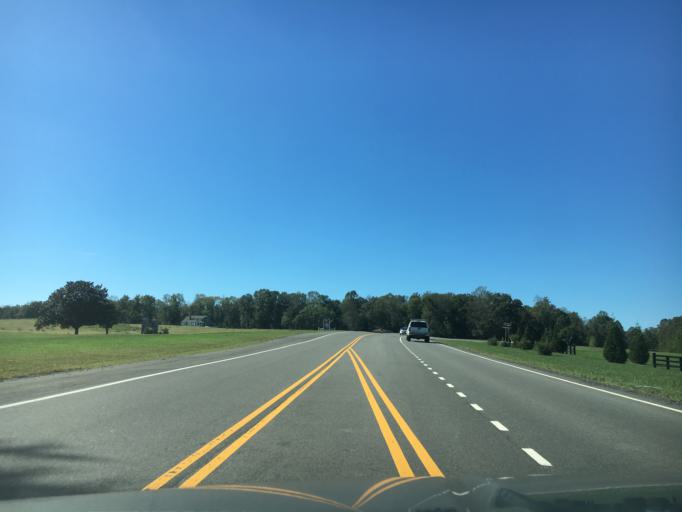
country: US
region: Virginia
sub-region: Goochland County
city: Goochland
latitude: 37.6985
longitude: -77.8304
